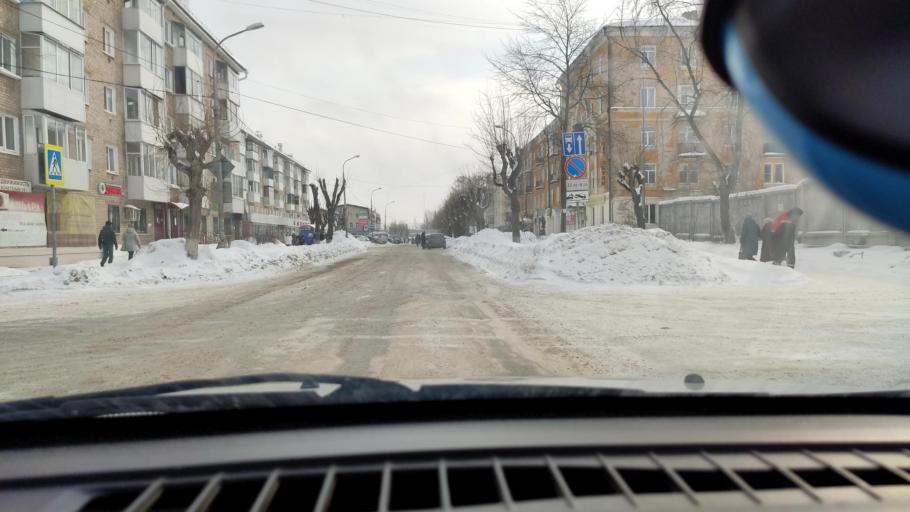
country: RU
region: Perm
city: Krasnokamsk
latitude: 58.0810
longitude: 55.7538
